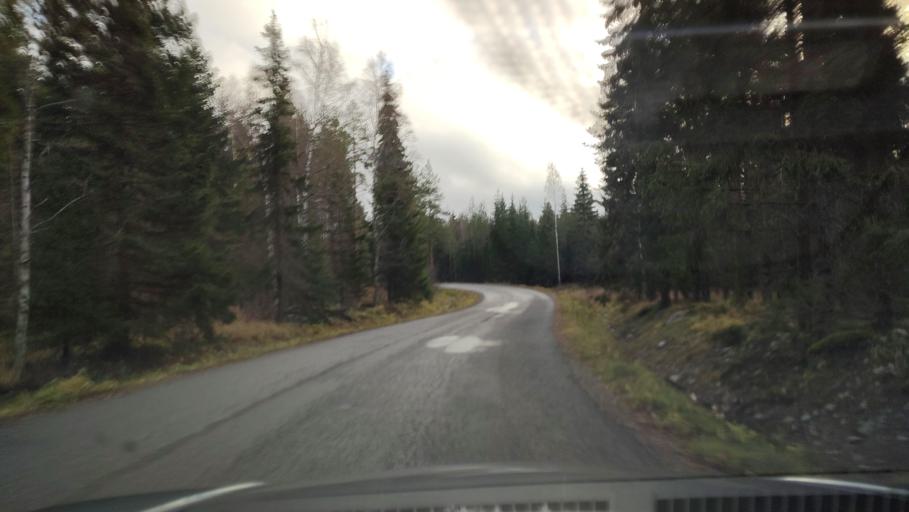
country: FI
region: Ostrobothnia
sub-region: Sydosterbotten
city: Kristinestad
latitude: 62.1544
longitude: 21.5273
